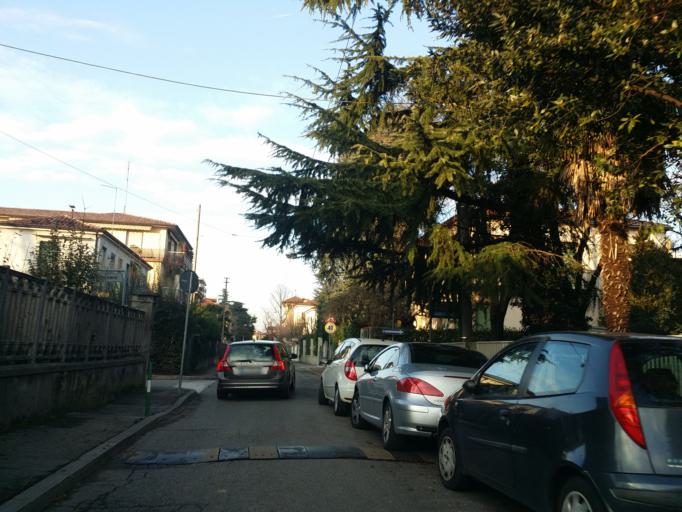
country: IT
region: Veneto
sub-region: Provincia di Padova
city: Padova
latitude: 45.4055
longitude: 11.8603
